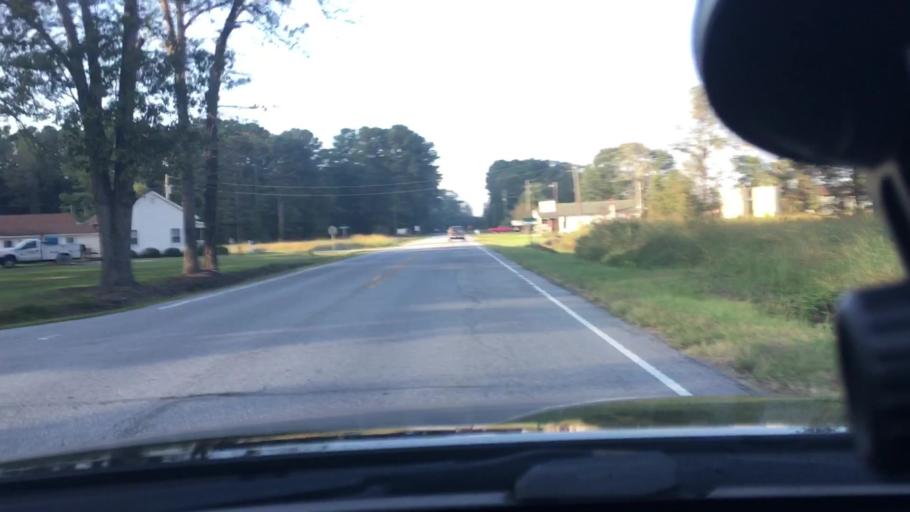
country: US
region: North Carolina
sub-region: Pitt County
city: Windsor
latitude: 35.4475
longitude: -77.2636
